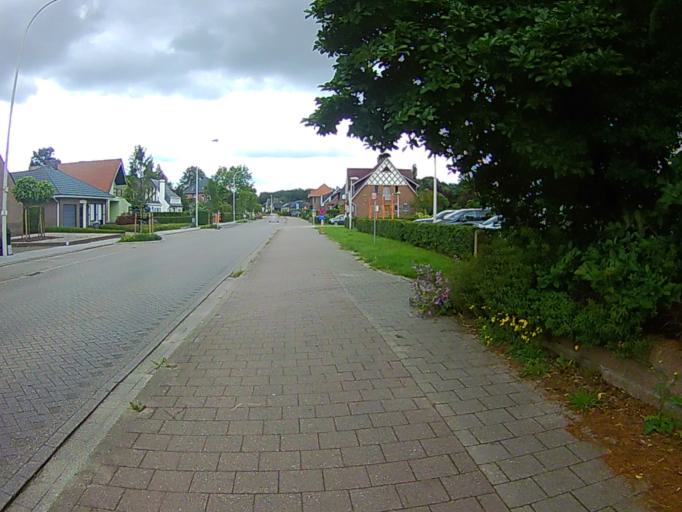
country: BE
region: Flanders
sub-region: Provincie Antwerpen
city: Berlaar
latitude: 51.1383
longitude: 4.6330
